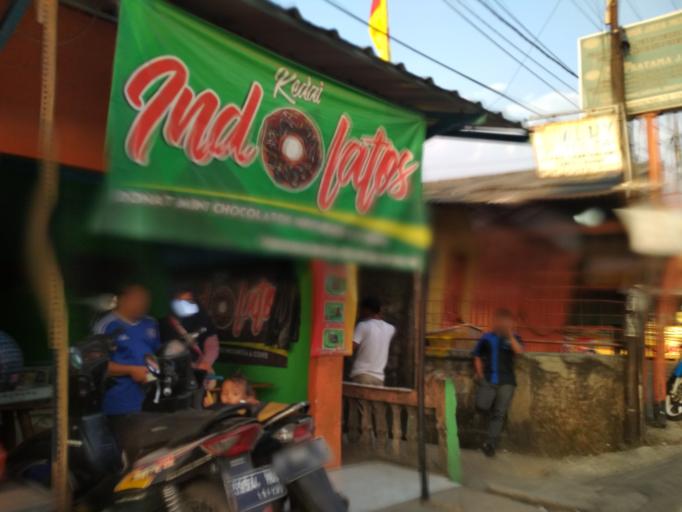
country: ID
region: West Java
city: Ciampea
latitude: -6.5596
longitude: 106.7130
